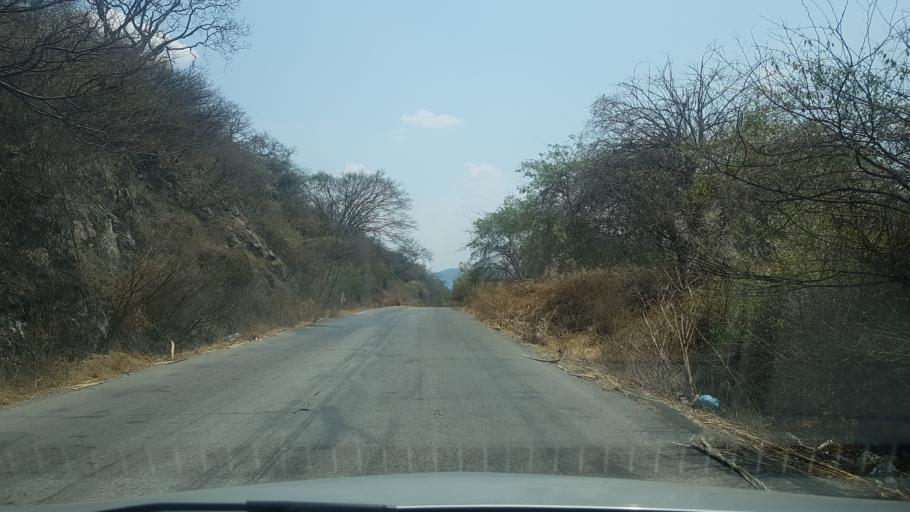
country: MX
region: Morelos
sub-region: Tlaltizapan de Zapata
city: Colonia Palo Prieto (Chipitongo)
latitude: 18.7782
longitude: -99.1059
